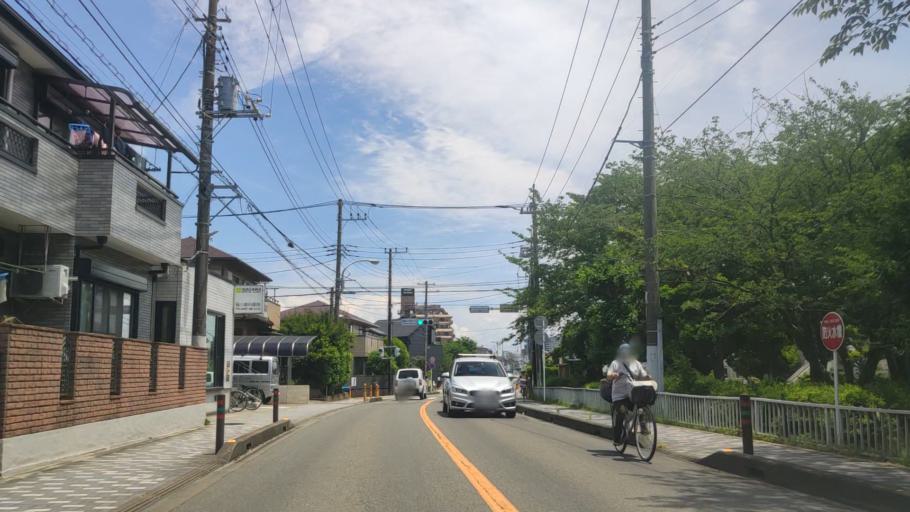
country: JP
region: Kanagawa
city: Chigasaki
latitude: 35.3376
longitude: 139.3882
